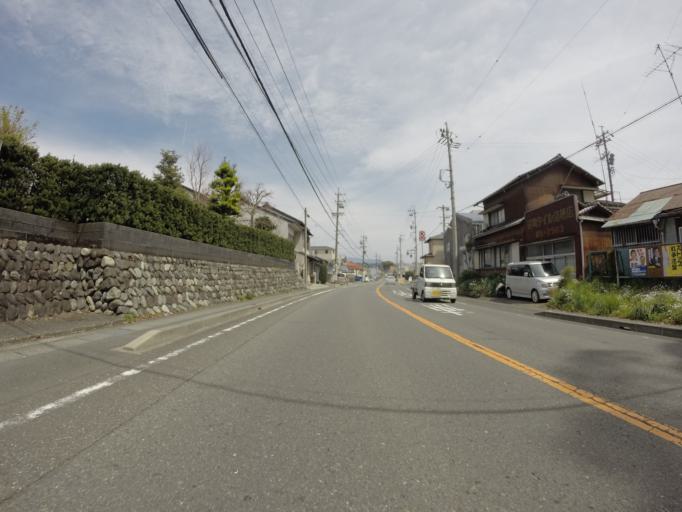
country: JP
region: Shizuoka
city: Fujinomiya
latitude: 35.1059
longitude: 138.5581
